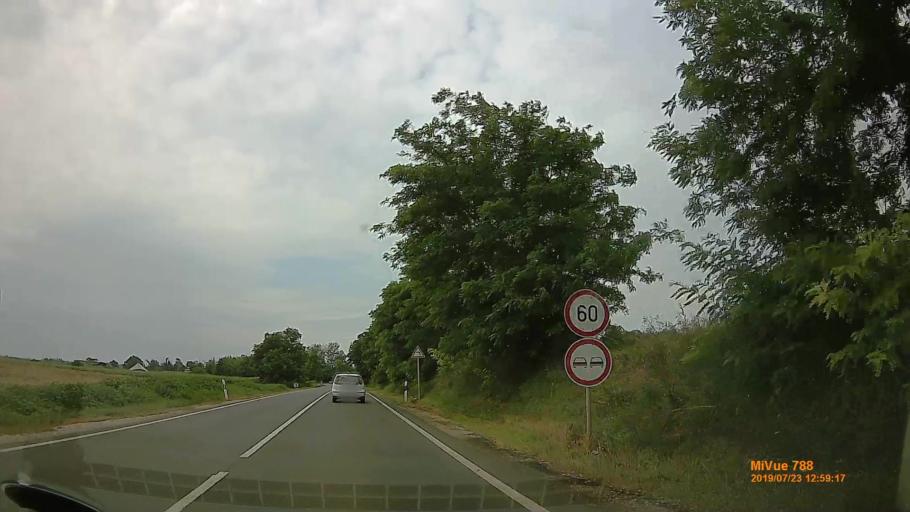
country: HU
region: Szabolcs-Szatmar-Bereg
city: Tiszalok
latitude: 47.9596
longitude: 21.4399
